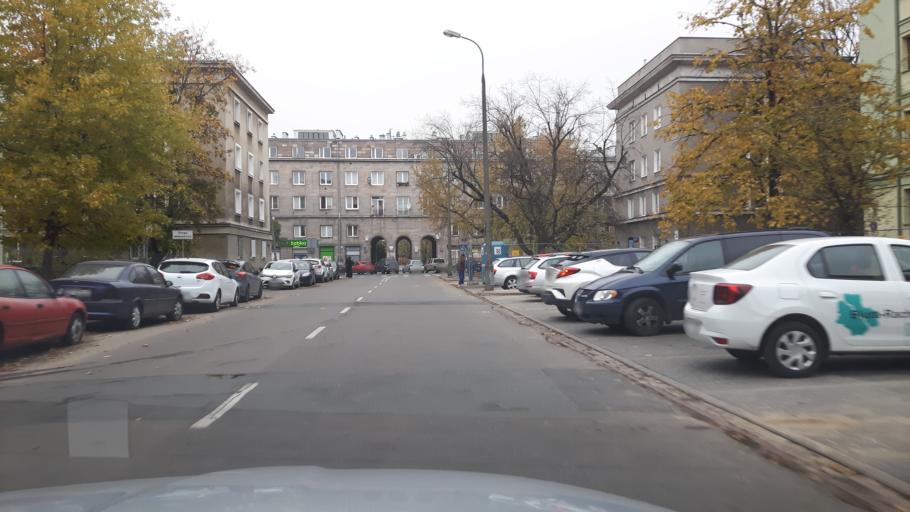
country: PL
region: Masovian Voivodeship
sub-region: Warszawa
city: Praga Polnoc
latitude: 52.2624
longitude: 21.0297
